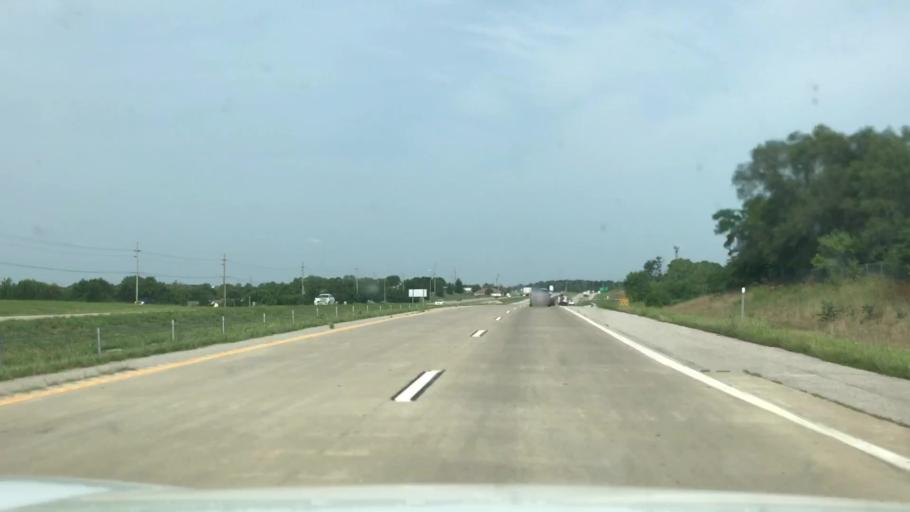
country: US
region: Missouri
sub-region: Saint Charles County
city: Dardenne Prairie
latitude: 38.7558
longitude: -90.7066
